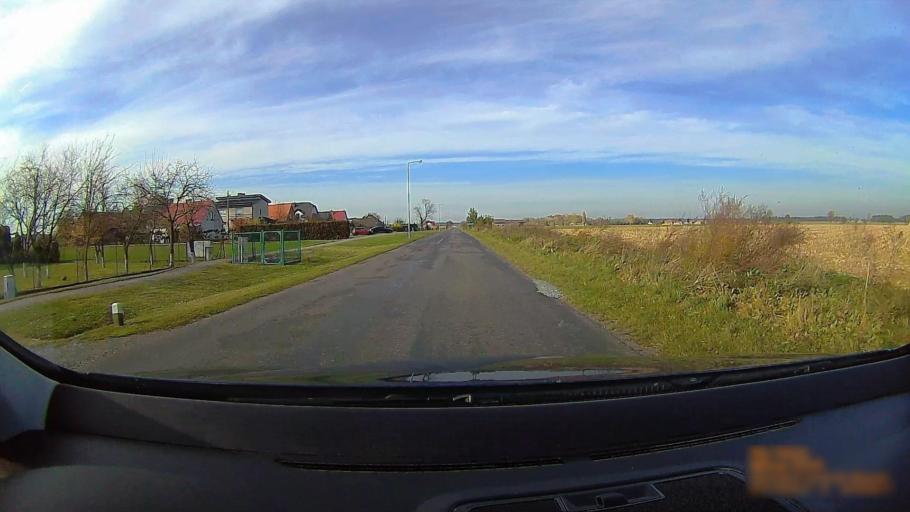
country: PL
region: Greater Poland Voivodeship
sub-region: Powiat ostrzeszowski
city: Doruchow
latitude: 51.4209
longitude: 18.0652
